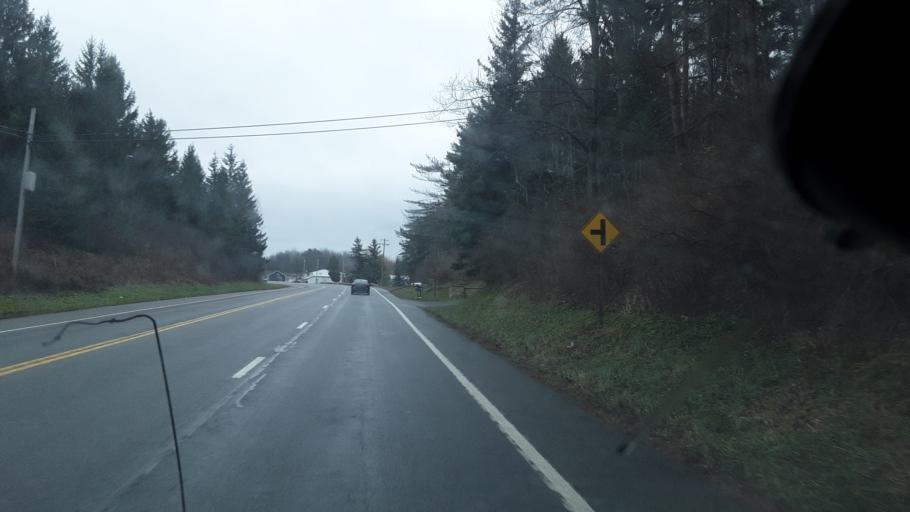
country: US
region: New York
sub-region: Erie County
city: Holland
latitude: 42.5928
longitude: -78.4961
